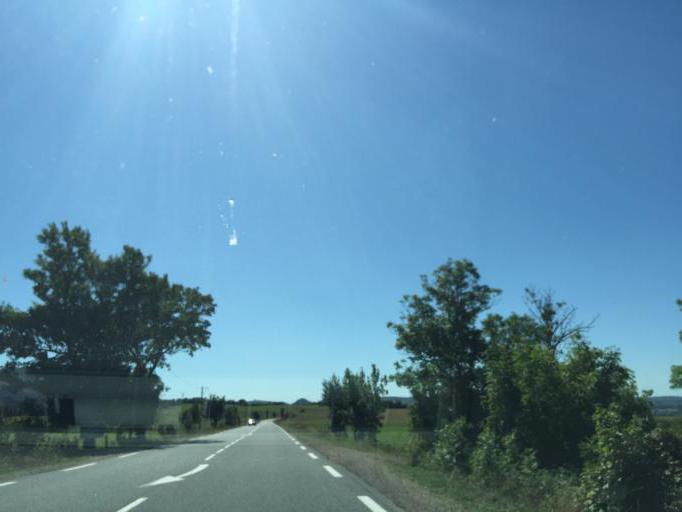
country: FR
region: Midi-Pyrenees
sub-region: Departement de l'Aveyron
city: Saint-Georges-de-Luzencon
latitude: 44.0111
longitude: 3.0130
